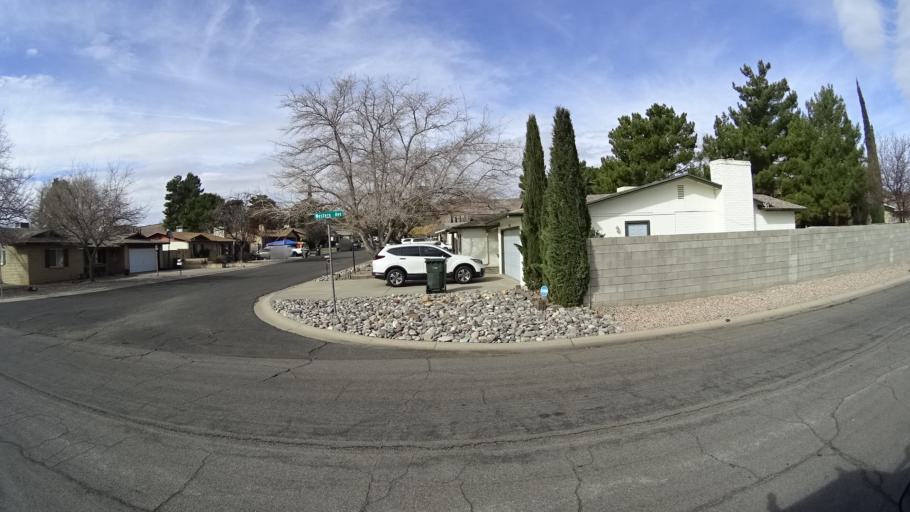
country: US
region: Arizona
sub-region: Mohave County
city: New Kingman-Butler
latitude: 35.2379
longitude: -114.0403
